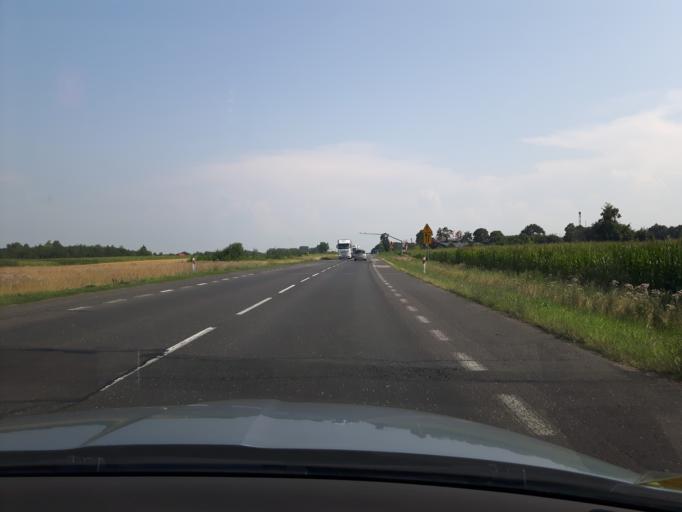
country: PL
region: Masovian Voivodeship
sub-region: Powiat plonski
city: Plonsk
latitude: 52.6887
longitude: 20.3561
